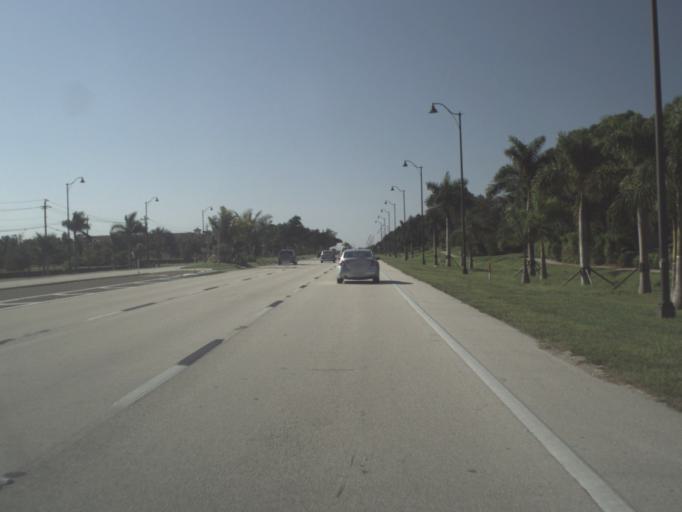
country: US
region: Florida
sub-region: Lee County
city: Bonita Springs
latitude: 26.3637
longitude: -81.8079
